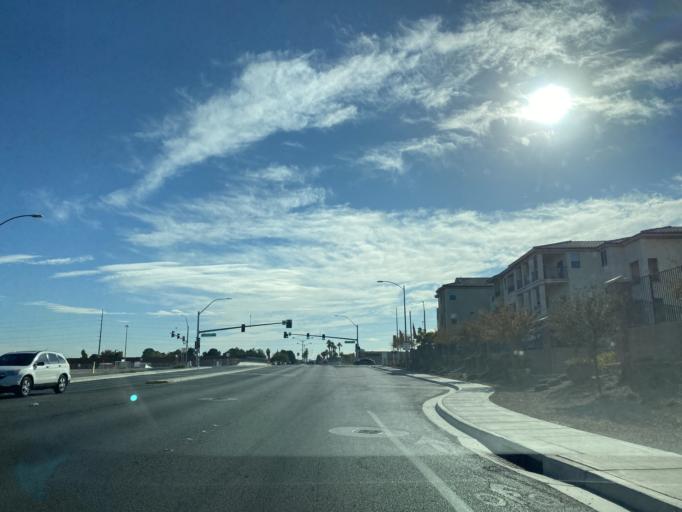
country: US
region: Nevada
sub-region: Clark County
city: Las Vegas
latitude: 36.2779
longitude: -115.2517
